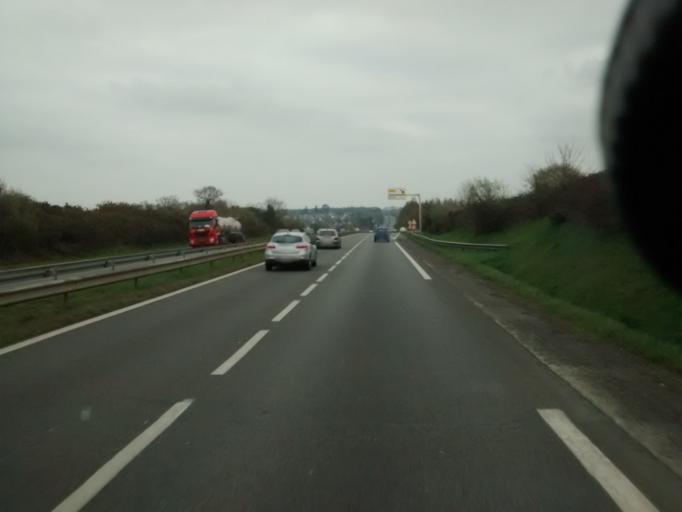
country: FR
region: Brittany
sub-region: Departement d'Ille-et-Vilaine
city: Saint-Gilles
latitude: 48.1536
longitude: -1.8027
